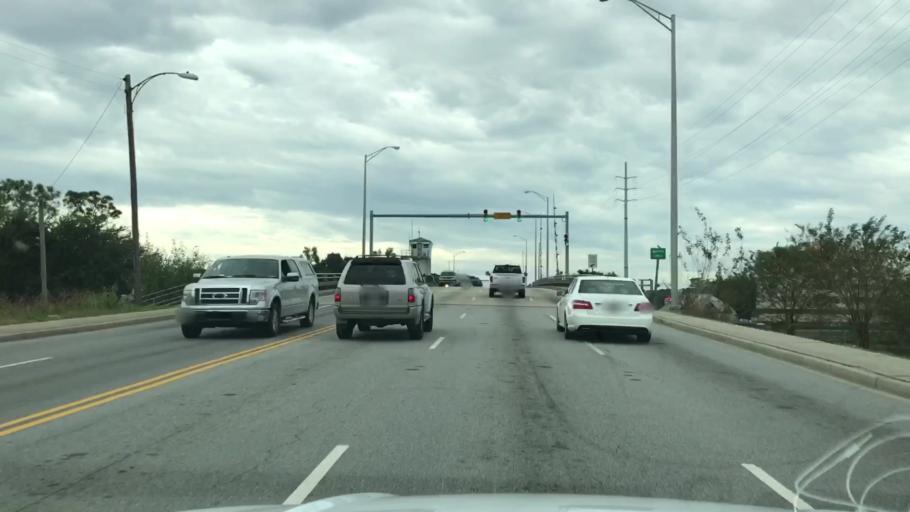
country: US
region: South Carolina
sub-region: Charleston County
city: Charleston
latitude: 32.7678
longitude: -79.9739
